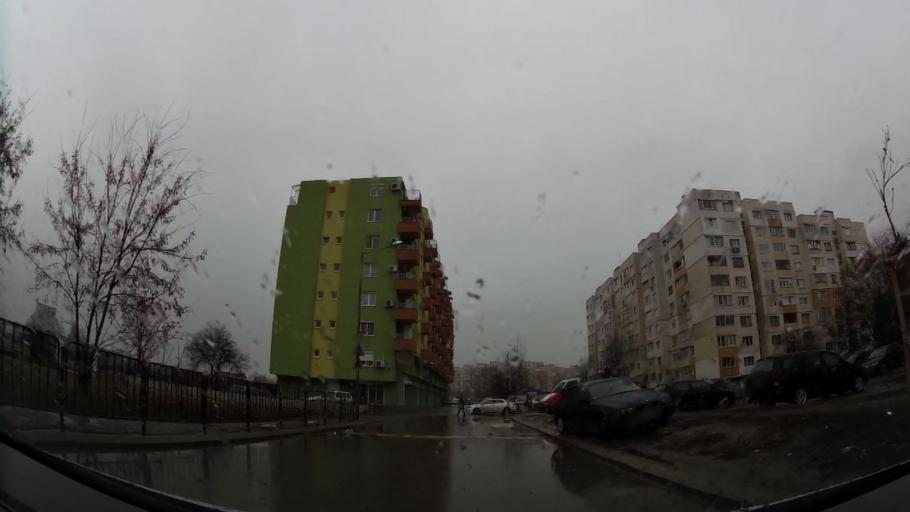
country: BG
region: Sofia-Capital
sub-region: Stolichna Obshtina
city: Sofia
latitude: 42.6451
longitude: 23.4101
